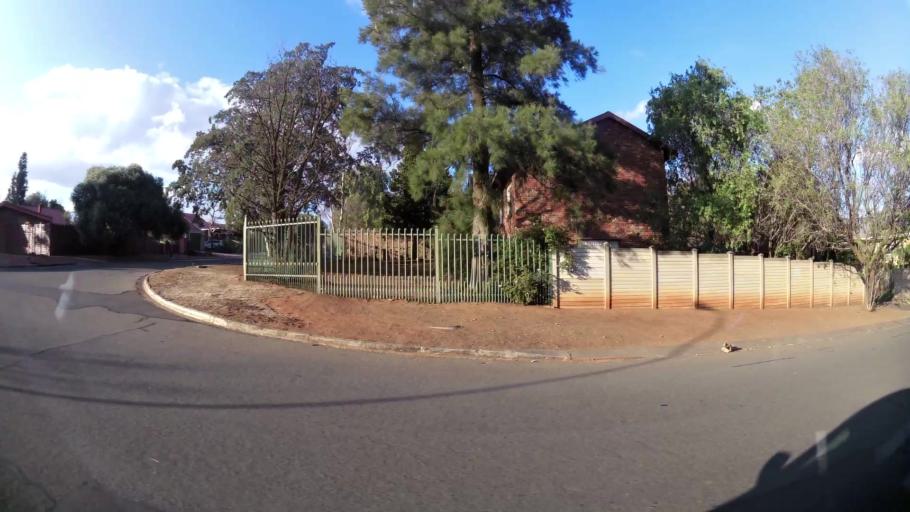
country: ZA
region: Orange Free State
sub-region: Mangaung Metropolitan Municipality
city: Bloemfontein
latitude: -29.1565
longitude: 26.1774
